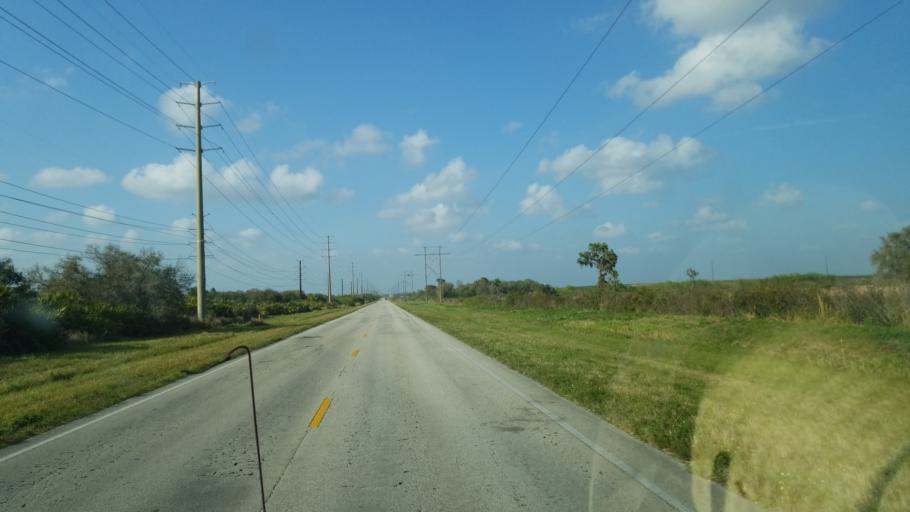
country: US
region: Florida
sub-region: Hardee County
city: Wauchula
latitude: 27.5543
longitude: -81.9323
